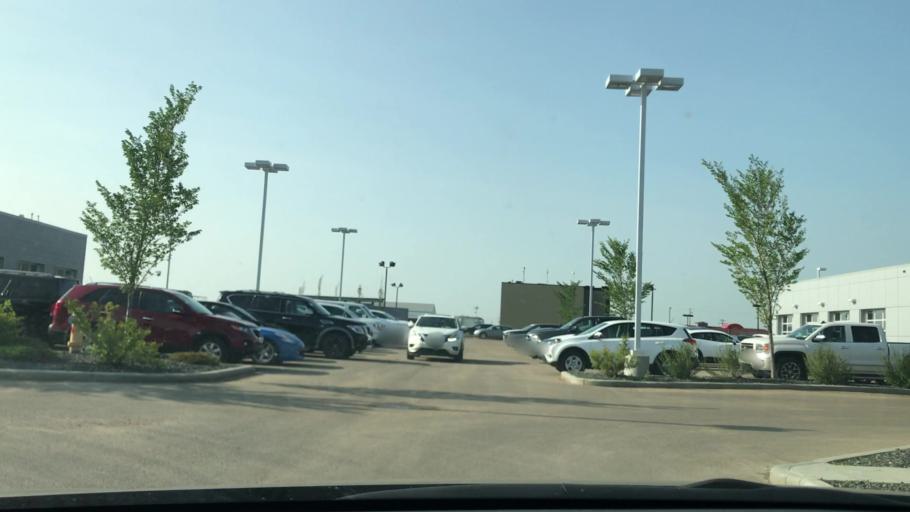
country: CA
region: Alberta
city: Leduc
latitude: 53.2789
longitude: -113.5464
